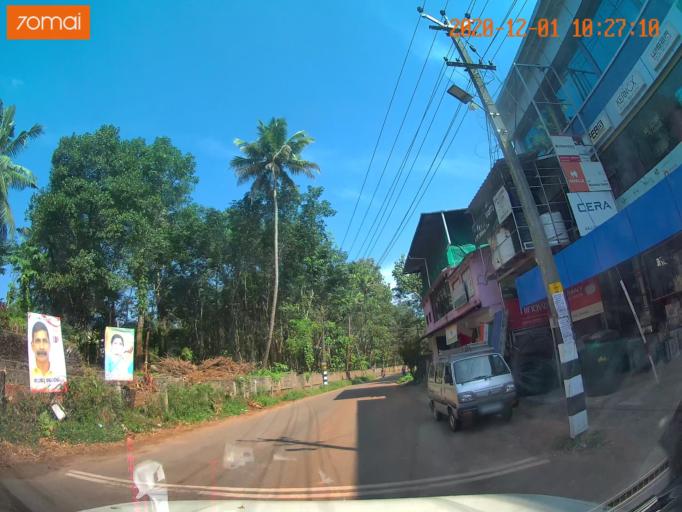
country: IN
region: Kerala
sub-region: Ernakulam
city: Ramamangalam
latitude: 9.9264
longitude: 76.5222
